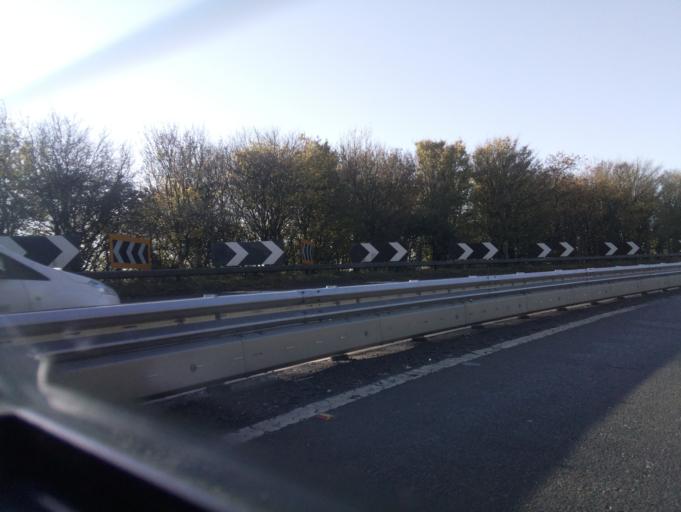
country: GB
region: England
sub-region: Somerset
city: Highbridge
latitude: 51.2356
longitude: -2.9441
